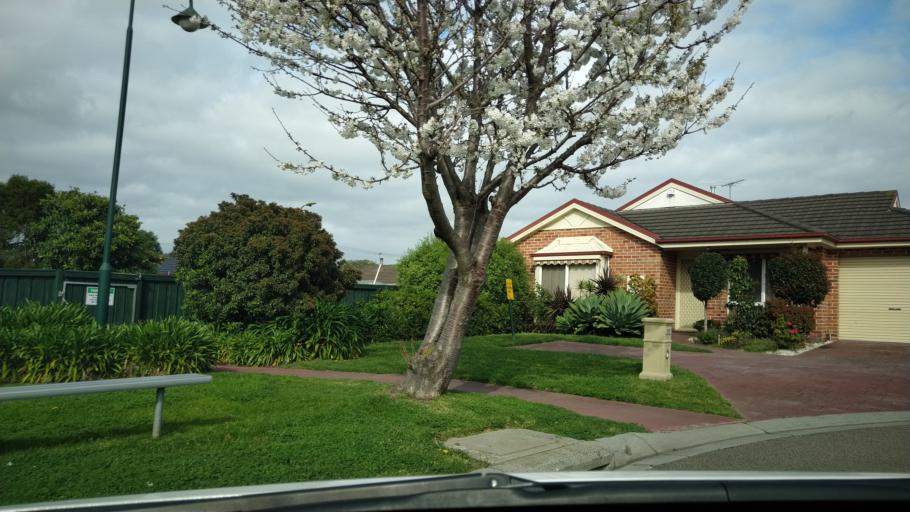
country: AU
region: Victoria
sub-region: Greater Dandenong
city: Keysborough
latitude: -37.9954
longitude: 145.1715
